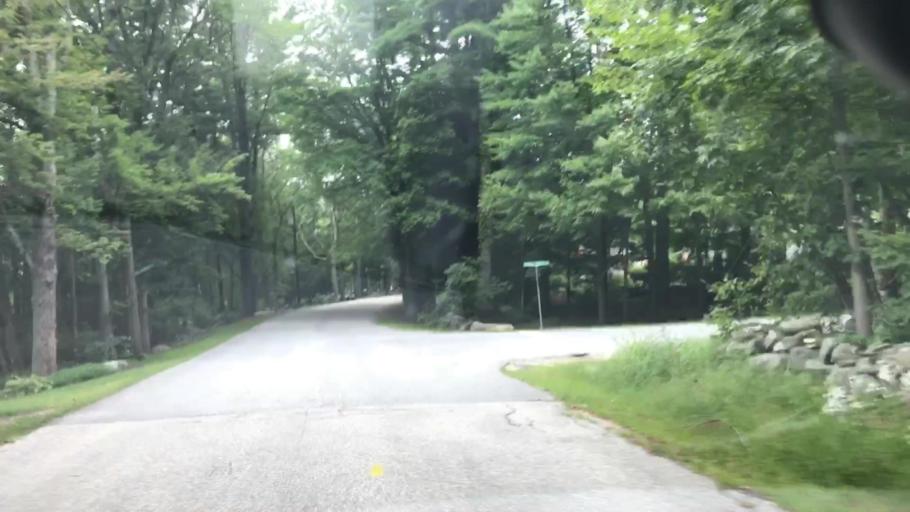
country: US
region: New Hampshire
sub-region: Hillsborough County
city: Milford
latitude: 42.8511
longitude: -71.6326
